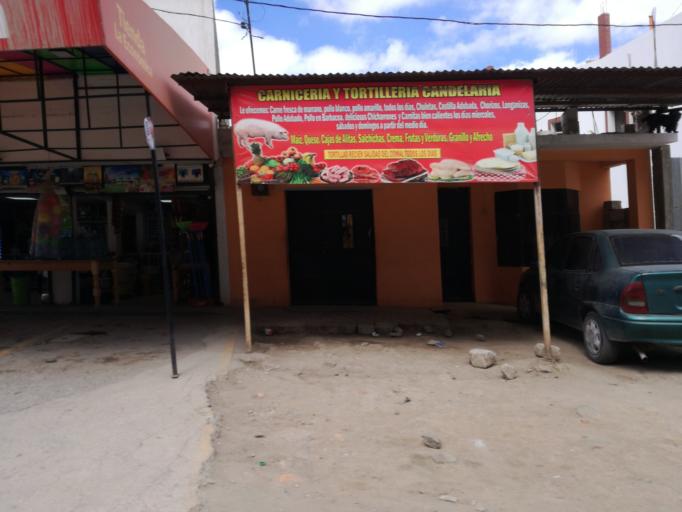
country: GT
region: Quetzaltenango
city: Quetzaltenango
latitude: 14.8209
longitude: -91.5366
